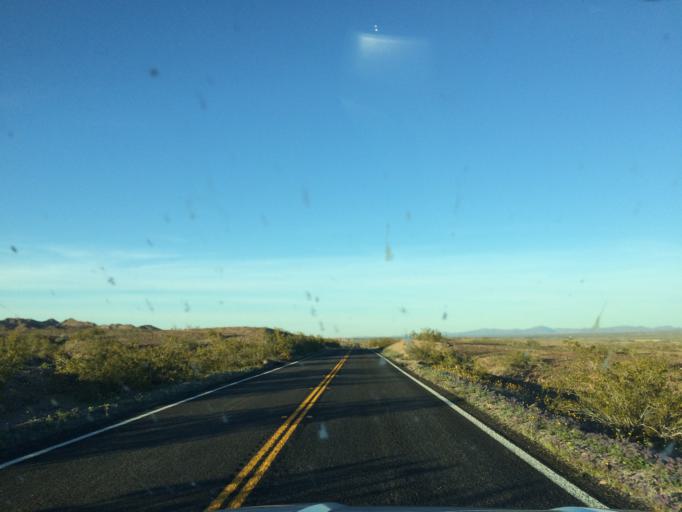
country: US
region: California
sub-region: Riverside County
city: Mesa Verde
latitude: 33.3031
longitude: -114.7445
